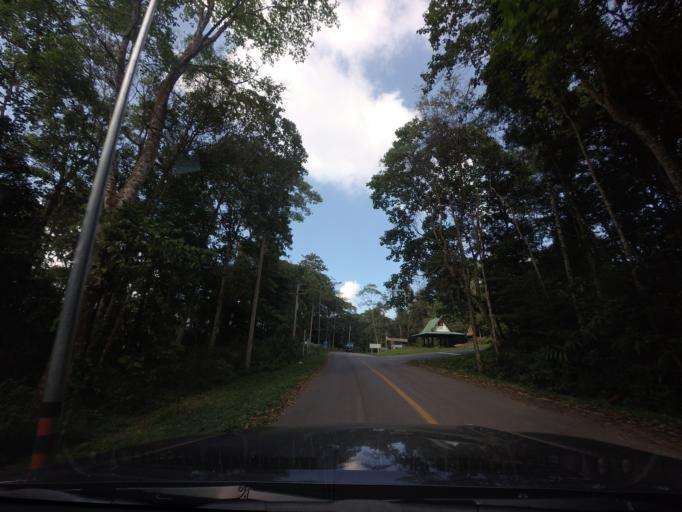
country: TH
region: Phitsanulok
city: Nakhon Thai
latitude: 16.9846
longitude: 101.0210
